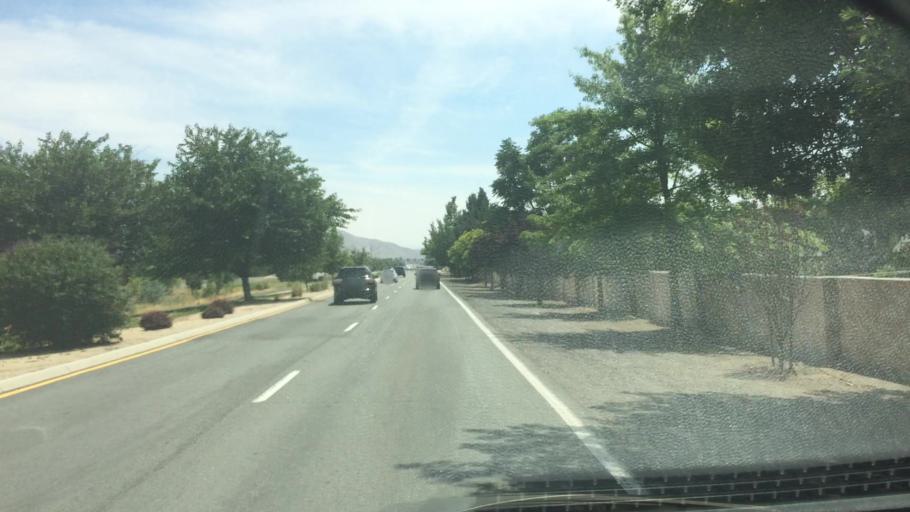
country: US
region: Nevada
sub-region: Washoe County
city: Sparks
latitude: 39.5458
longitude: -119.7155
